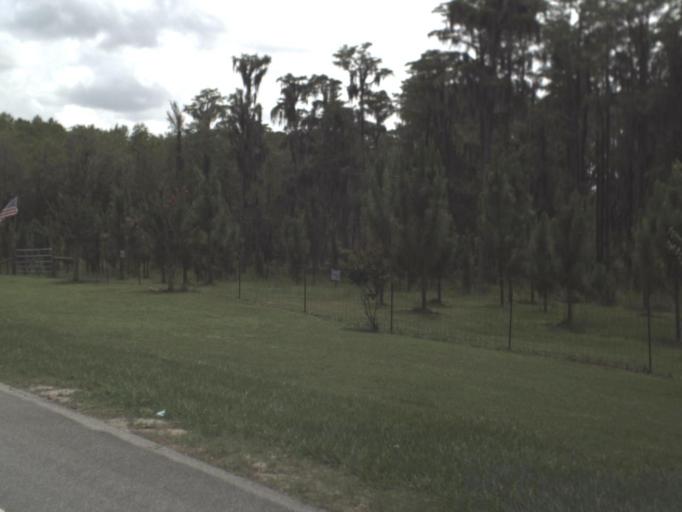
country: US
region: Florida
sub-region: Madison County
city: Madison
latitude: 30.5481
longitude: -83.4257
